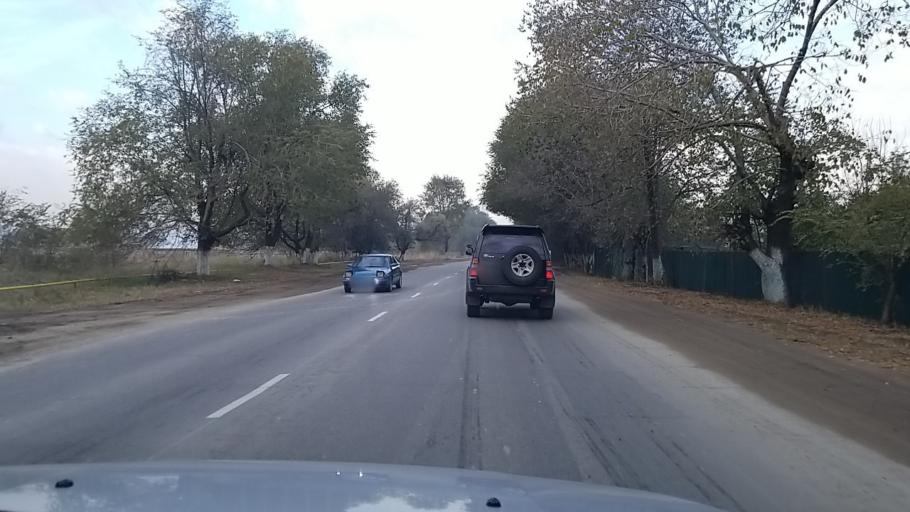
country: KZ
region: Almaty Oblysy
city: Burunday
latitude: 43.3593
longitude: 76.7538
